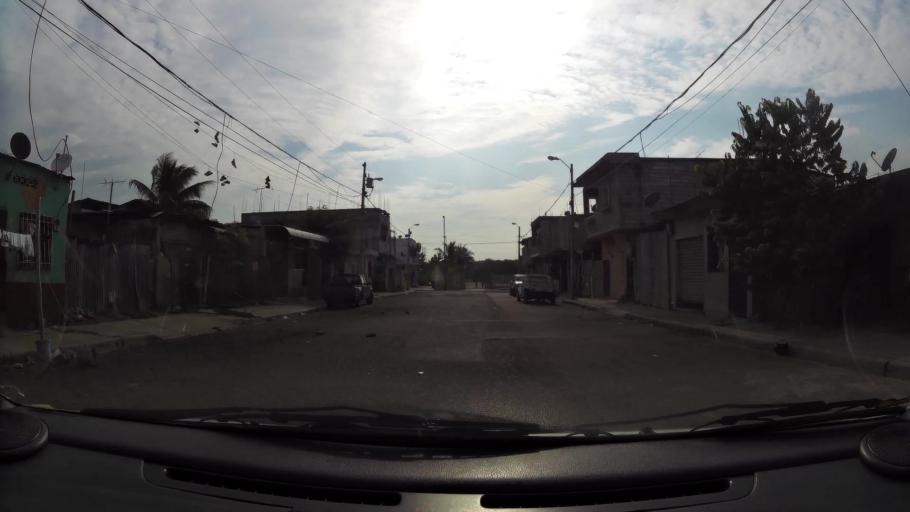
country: EC
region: Guayas
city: Guayaquil
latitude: -2.2474
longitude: -79.9082
